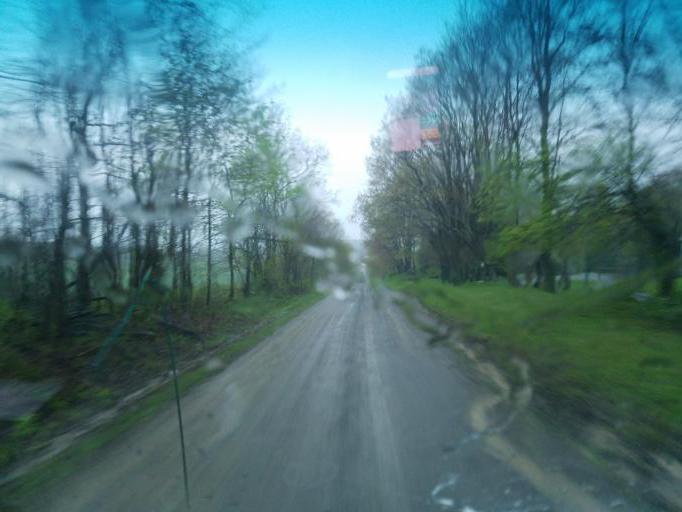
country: US
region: Pennsylvania
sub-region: Tioga County
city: Westfield
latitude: 41.9205
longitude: -77.7326
